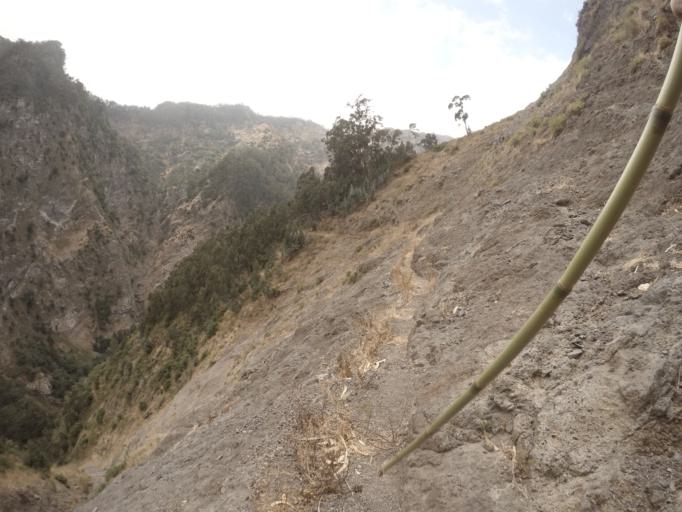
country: PT
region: Madeira
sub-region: Camara de Lobos
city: Curral das Freiras
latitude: 32.7038
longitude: -16.9664
